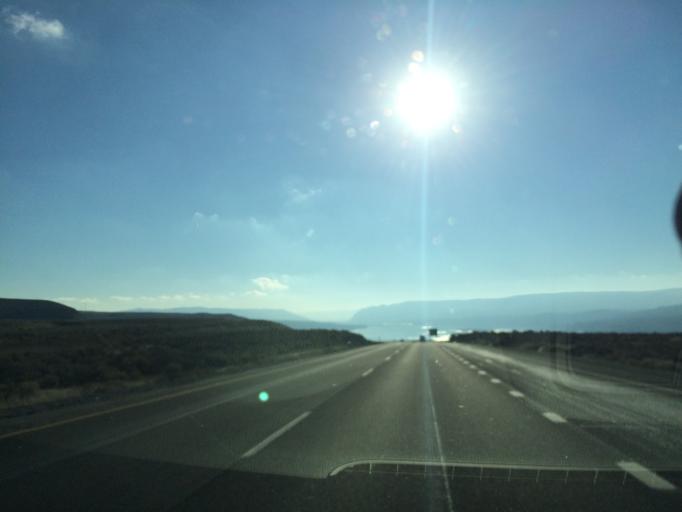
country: US
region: Washington
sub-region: Grant County
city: Mattawa
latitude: 46.9702
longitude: -119.9681
